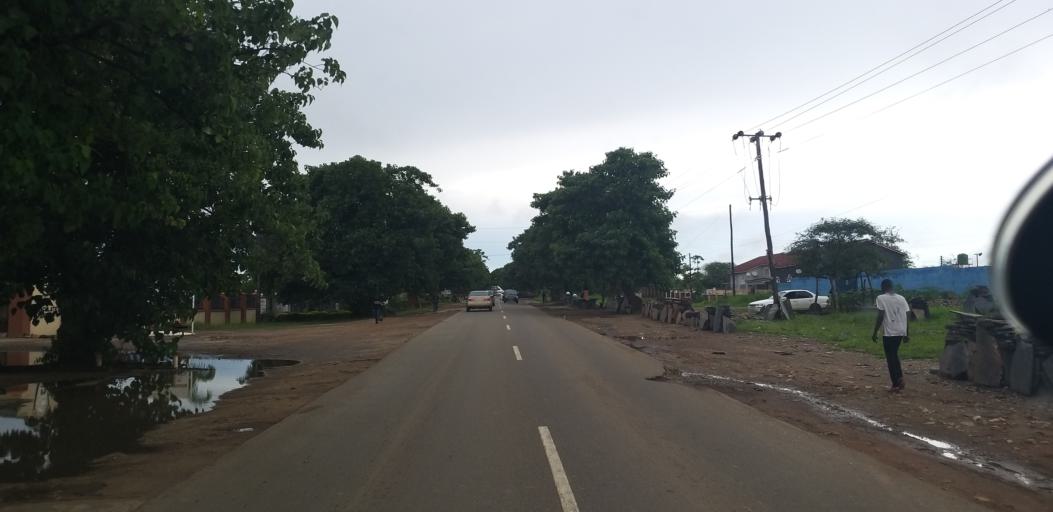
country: ZM
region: Lusaka
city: Lusaka
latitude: -15.4376
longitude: 28.3572
